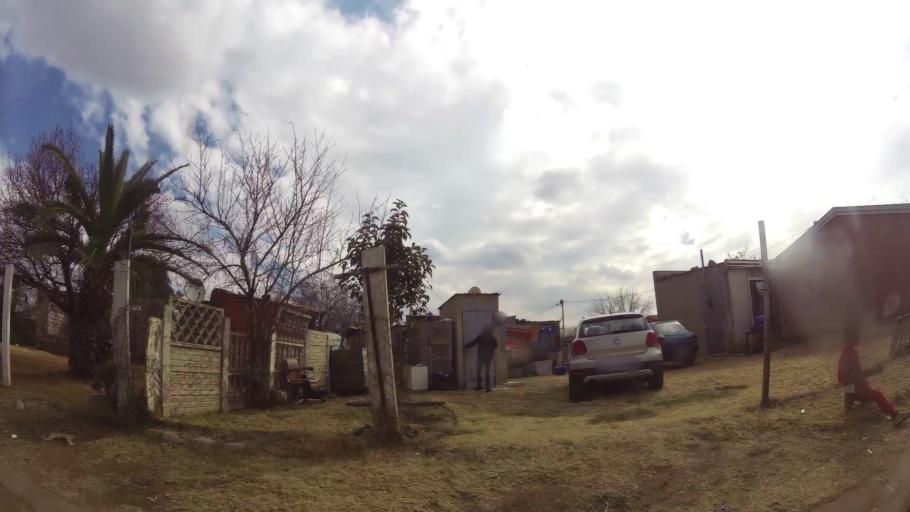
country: ZA
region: Gauteng
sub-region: Ekurhuleni Metropolitan Municipality
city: Germiston
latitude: -26.4070
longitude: 28.1664
